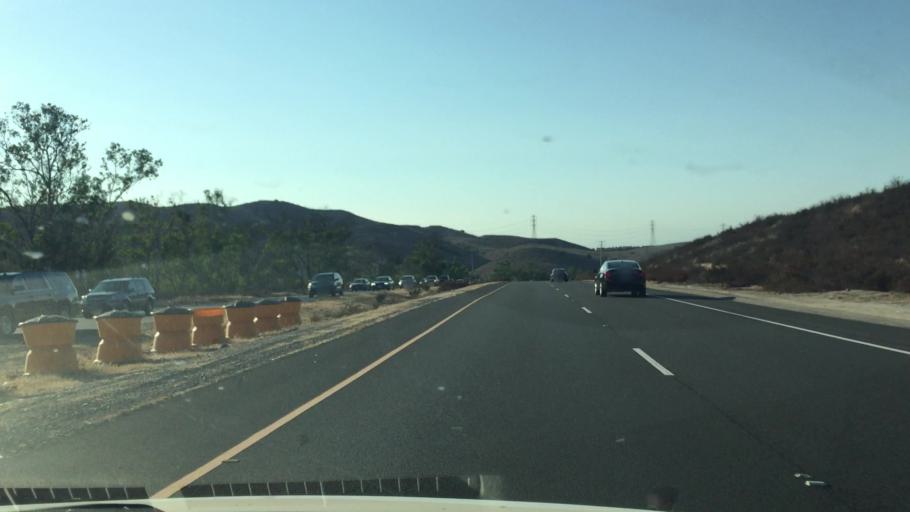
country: US
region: California
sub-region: Orange County
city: Laguna Woods
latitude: 33.6260
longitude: -117.7576
